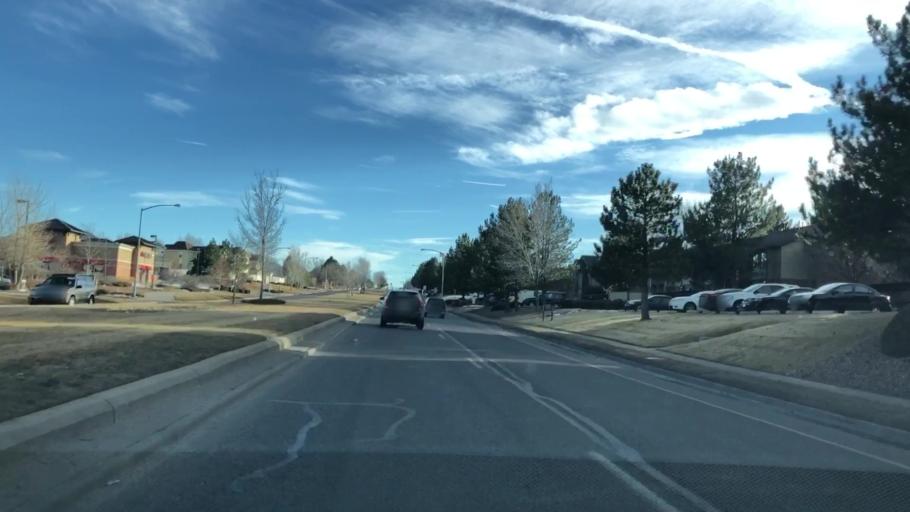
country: US
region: Colorado
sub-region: Adams County
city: Aurora
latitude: 39.6948
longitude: -104.7912
